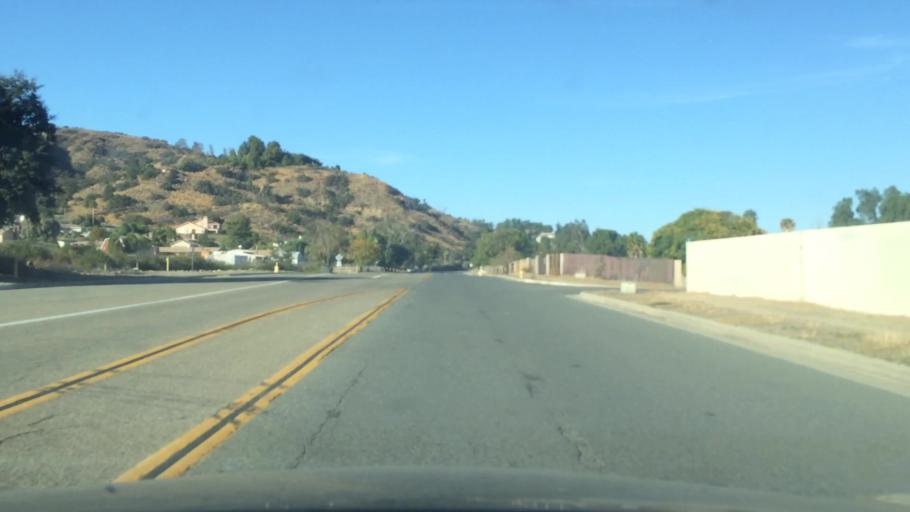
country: US
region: California
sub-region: Riverside County
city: Lakeland Village
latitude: 33.6755
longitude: -117.3984
